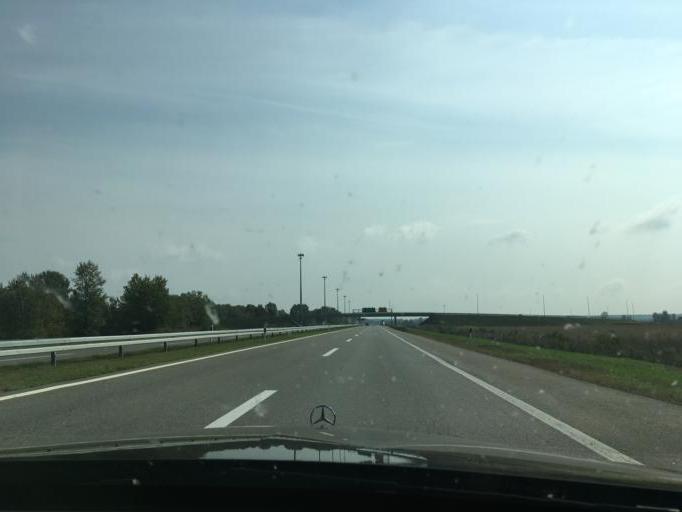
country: HR
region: Vukovarsko-Srijemska
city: Zupanja
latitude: 45.1034
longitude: 18.7108
